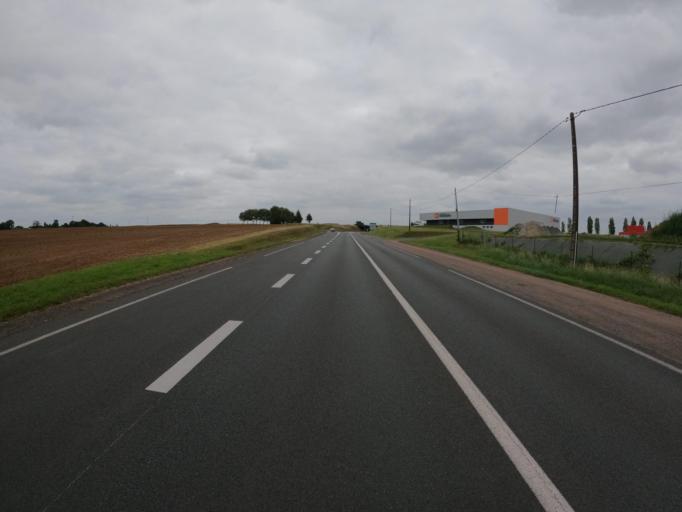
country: FR
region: Pays de la Loire
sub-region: Departement de la Vendee
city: Serigne
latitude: 46.4689
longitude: -0.8507
